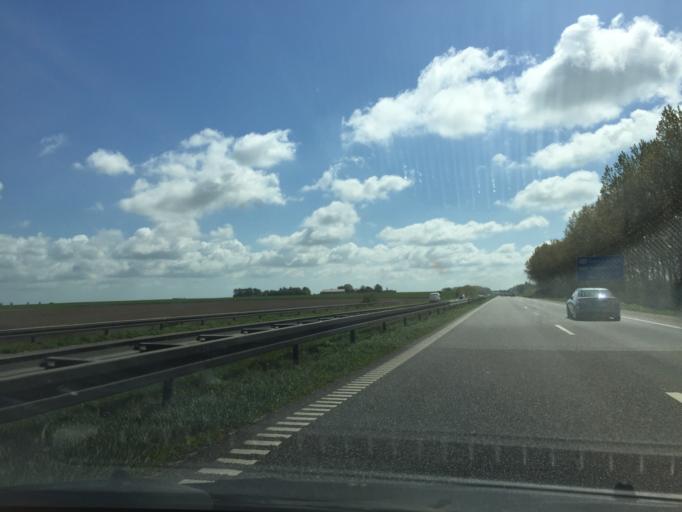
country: DK
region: Zealand
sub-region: Guldborgsund Kommune
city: Norre Alslev
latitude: 54.9077
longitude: 11.9272
